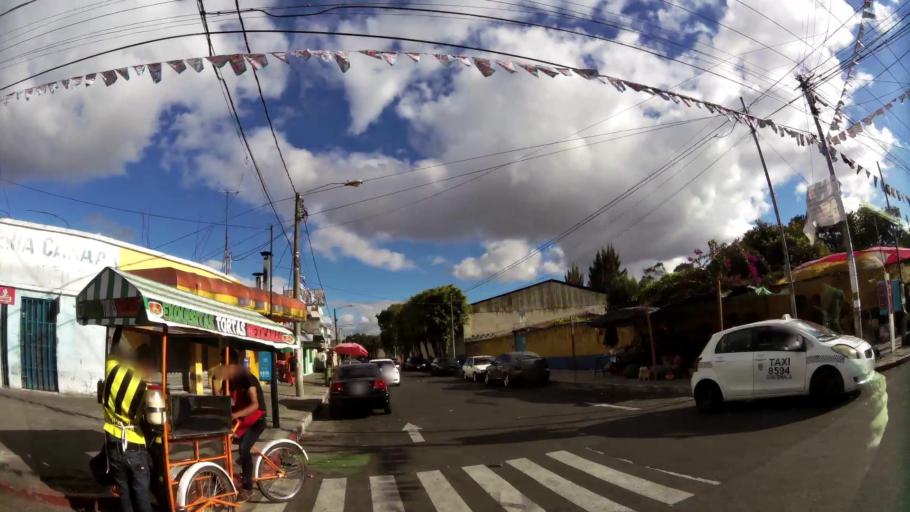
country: GT
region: Guatemala
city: Guatemala City
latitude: 14.6106
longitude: -90.5494
